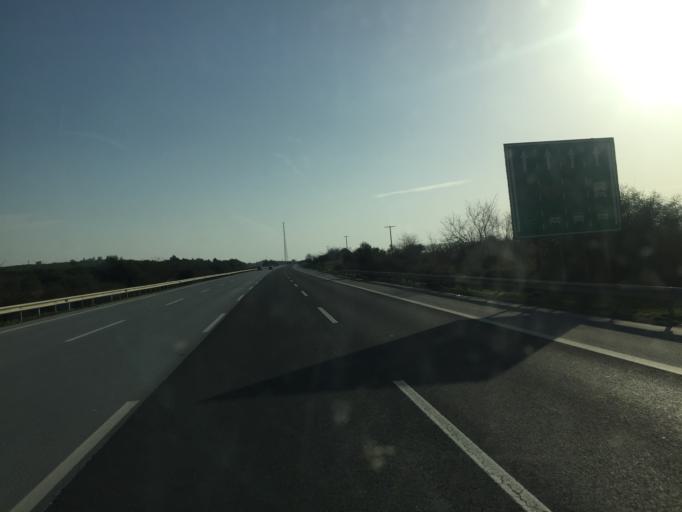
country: TR
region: Mersin
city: Yenice
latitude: 37.0233
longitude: 35.0726
